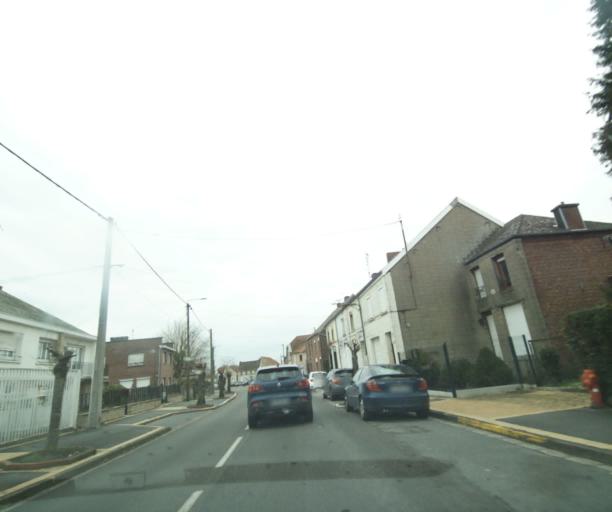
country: FR
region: Nord-Pas-de-Calais
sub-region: Departement du Nord
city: Quarouble
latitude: 50.3937
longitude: 3.6191
